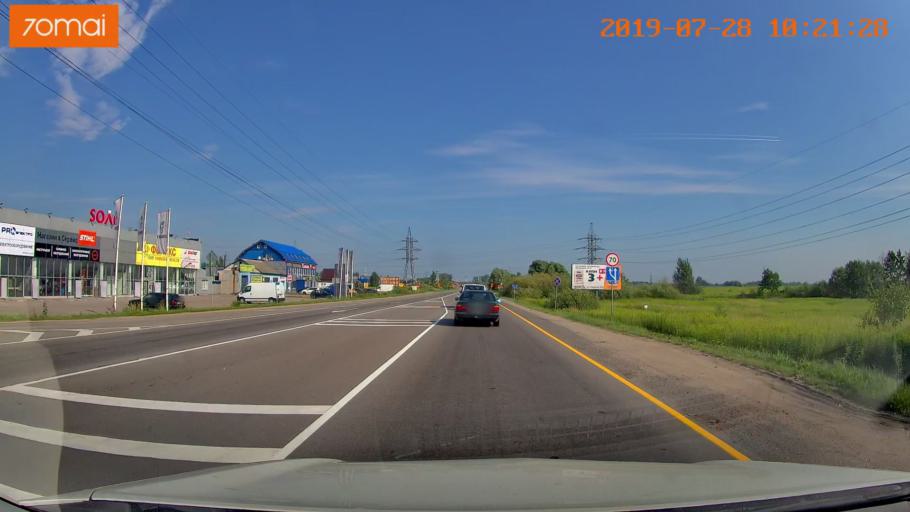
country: RU
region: Kaliningrad
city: Maloye Isakovo
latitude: 54.7573
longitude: 20.5641
